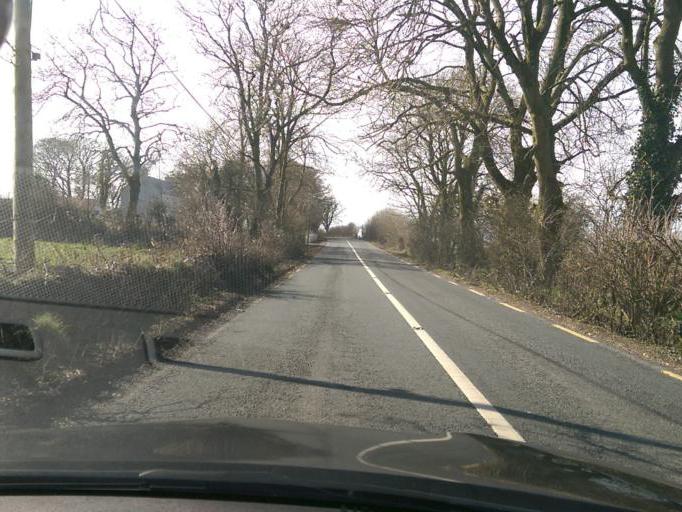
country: IE
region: Connaught
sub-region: County Galway
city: Athenry
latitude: 53.4740
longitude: -8.6277
